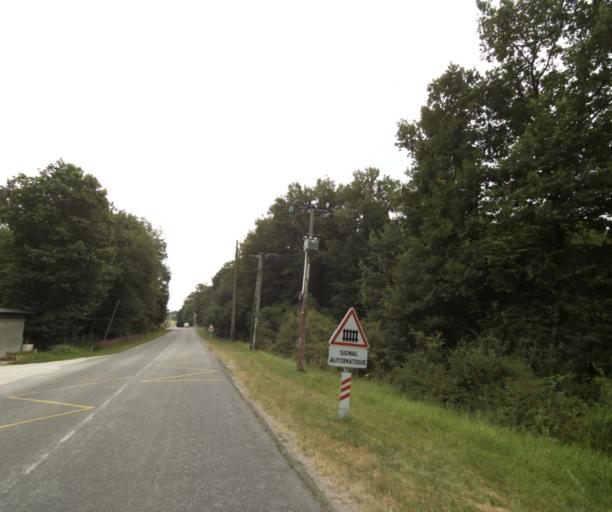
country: FR
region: Centre
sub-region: Departement du Loiret
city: Marigny-les-Usages
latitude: 47.9610
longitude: 1.9993
